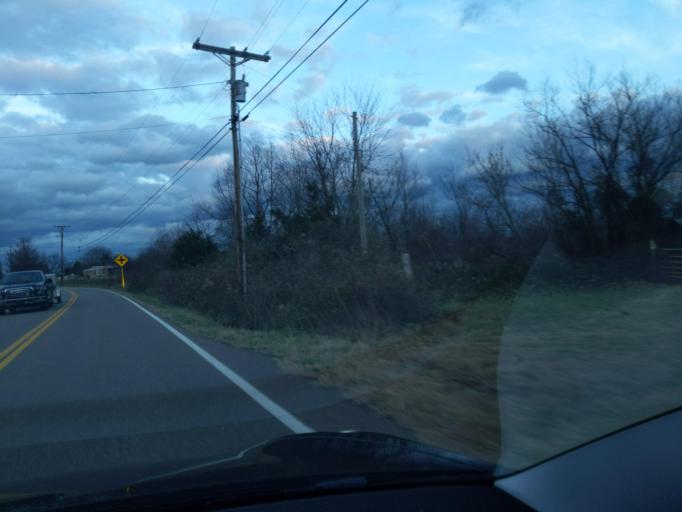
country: US
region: Tennessee
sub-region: Jefferson County
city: Dandridge
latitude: 36.0815
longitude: -83.3744
